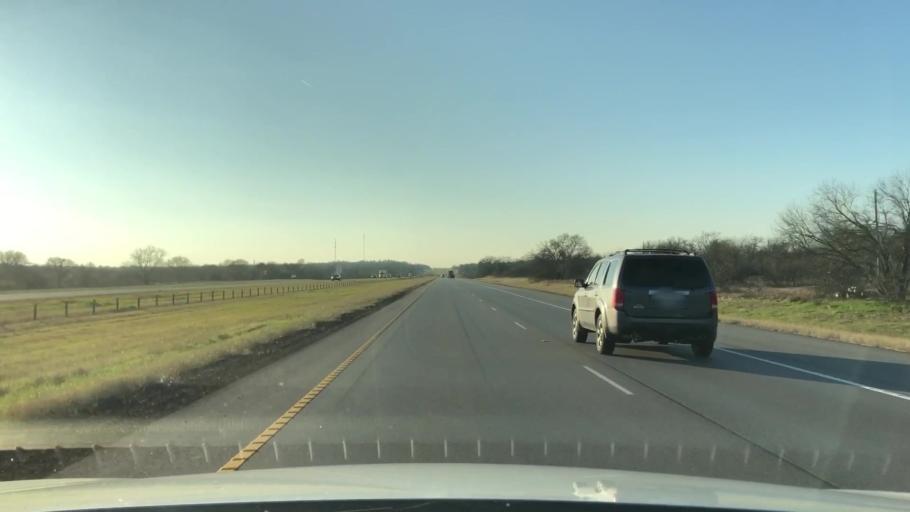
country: US
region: Texas
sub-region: Caldwell County
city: Luling
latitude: 29.6516
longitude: -97.5229
